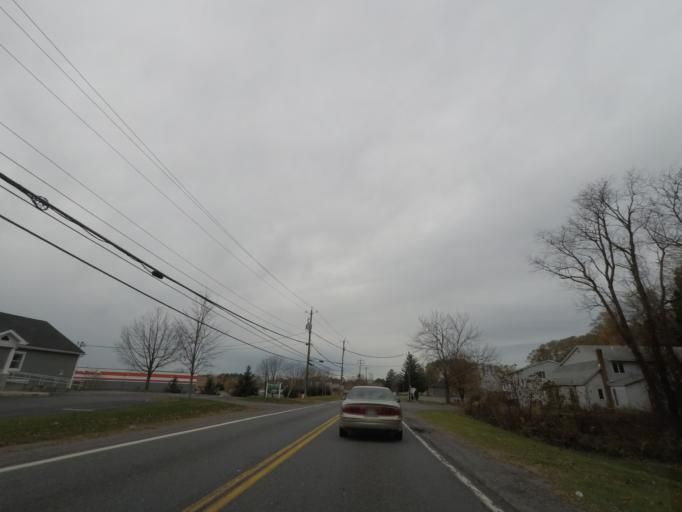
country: US
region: New York
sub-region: Saratoga County
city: Country Knolls
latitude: 42.8642
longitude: -73.7659
